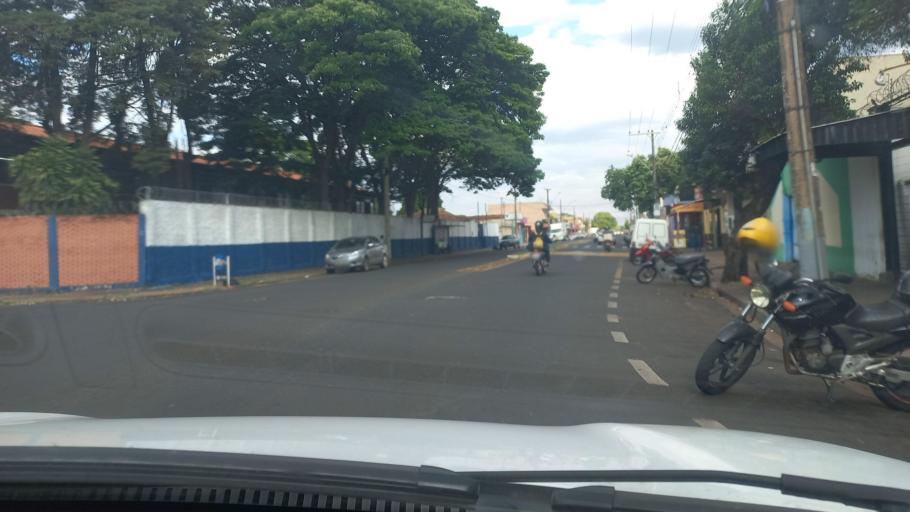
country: BR
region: Minas Gerais
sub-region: Uberaba
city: Uberaba
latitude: -19.7344
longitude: -47.9204
